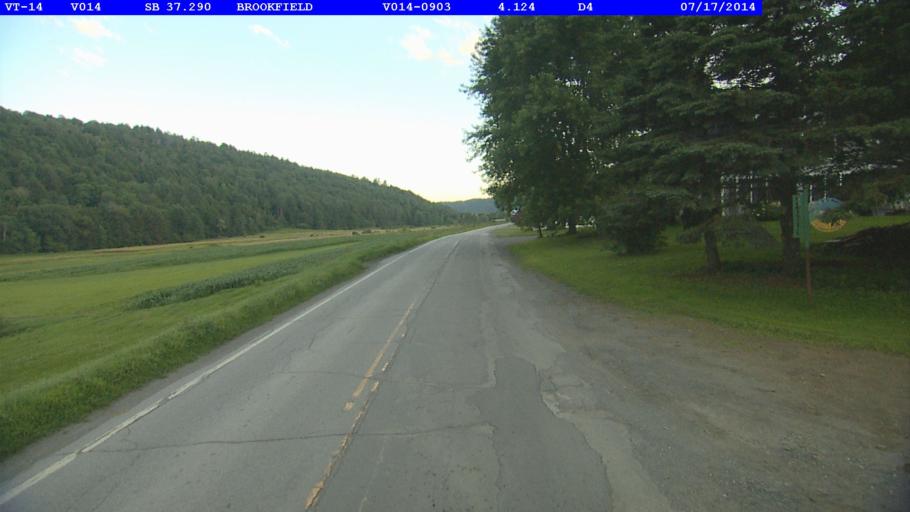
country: US
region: Vermont
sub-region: Orange County
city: Williamstown
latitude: 44.0363
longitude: -72.5692
